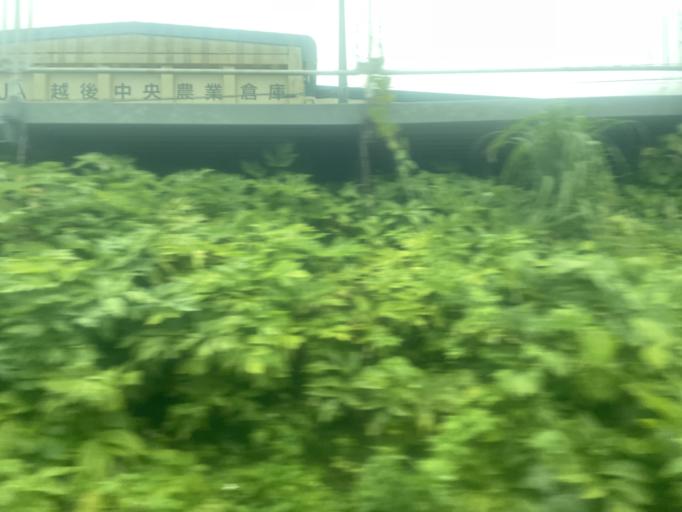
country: JP
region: Niigata
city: Yoshida-kasugacho
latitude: 37.6950
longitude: 138.8479
